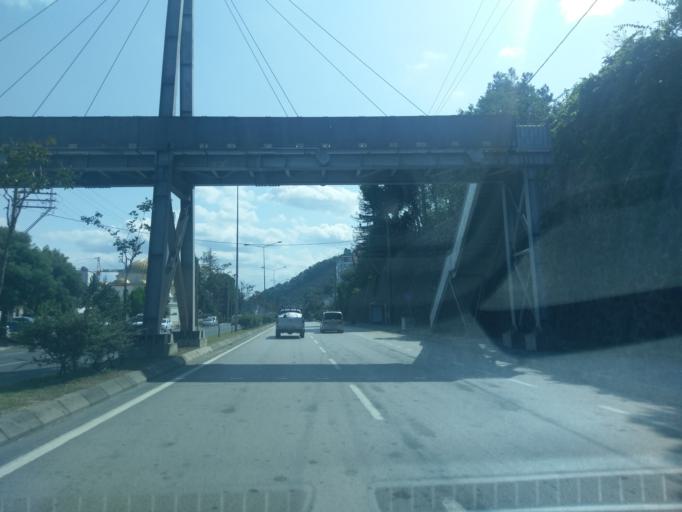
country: TR
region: Ordu
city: Ordu
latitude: 41.0045
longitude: 37.8701
